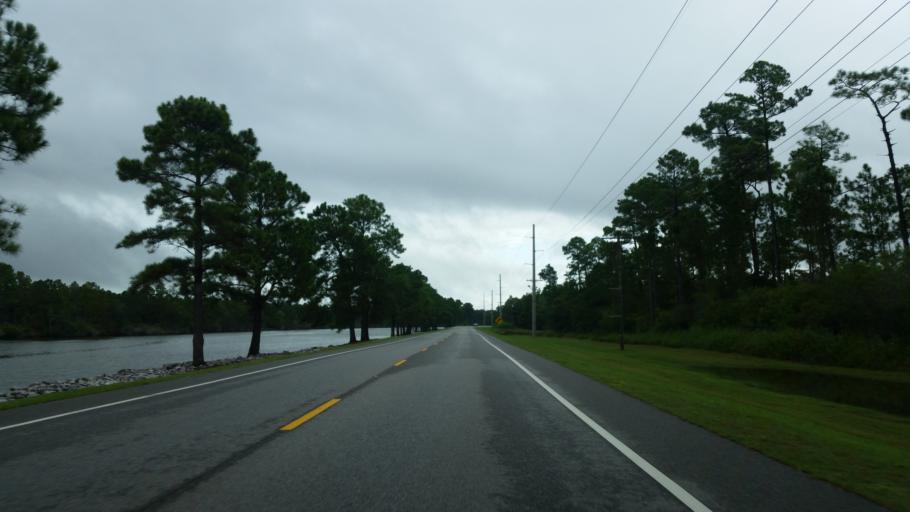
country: US
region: Alabama
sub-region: Baldwin County
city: Gulf Shores
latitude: 30.2838
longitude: -87.6469
